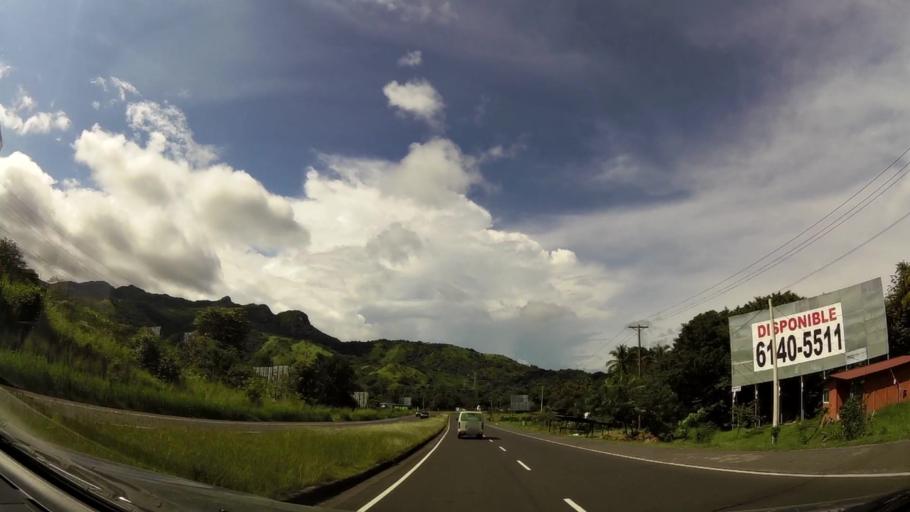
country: PA
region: Panama
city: Bejuco
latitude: 8.6575
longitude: -79.8715
